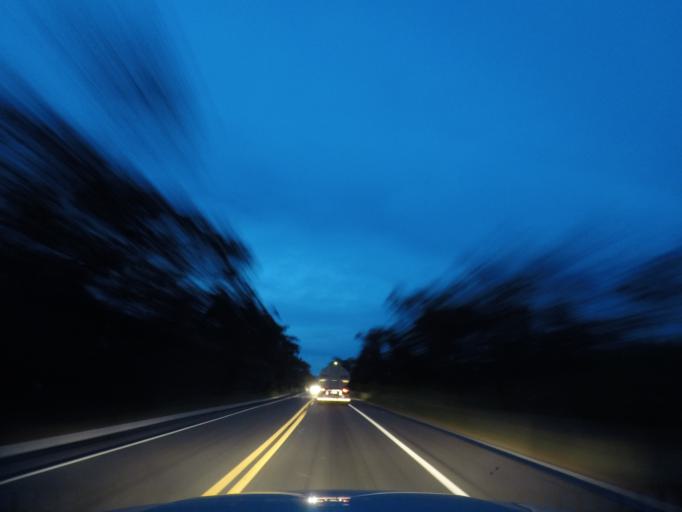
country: BR
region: Bahia
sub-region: Andarai
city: Vera Cruz
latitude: -12.4958
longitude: -41.3336
